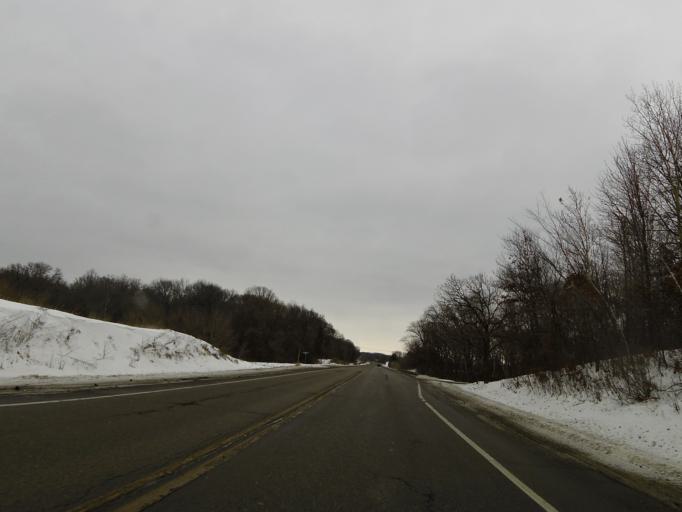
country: US
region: Minnesota
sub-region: Washington County
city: Stillwater
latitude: 45.0715
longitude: -92.7726
